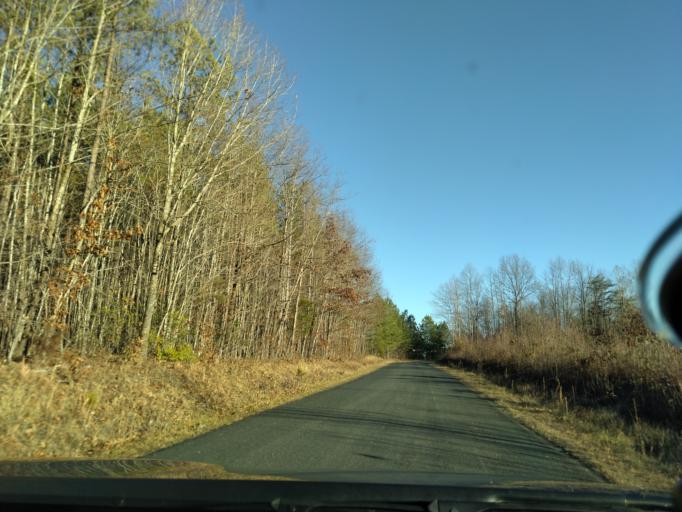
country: US
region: Virginia
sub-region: Buckingham County
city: Buckingham
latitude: 37.3702
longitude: -78.6193
